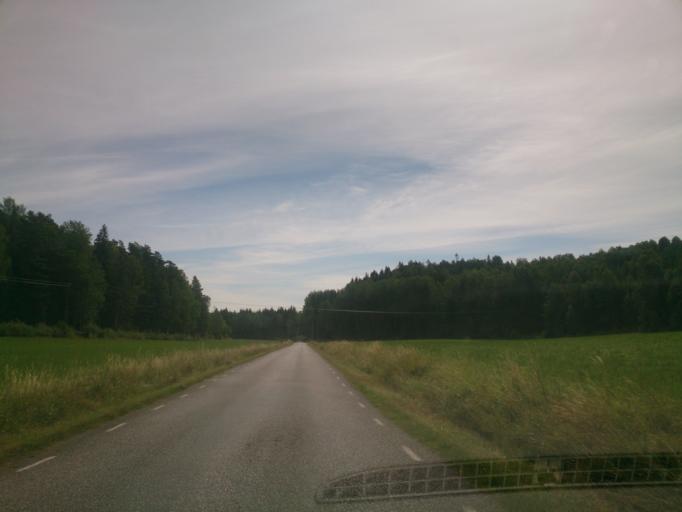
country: SE
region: OEstergoetland
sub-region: Atvidabergs Kommun
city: Atvidaberg
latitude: 58.3049
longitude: 16.0844
